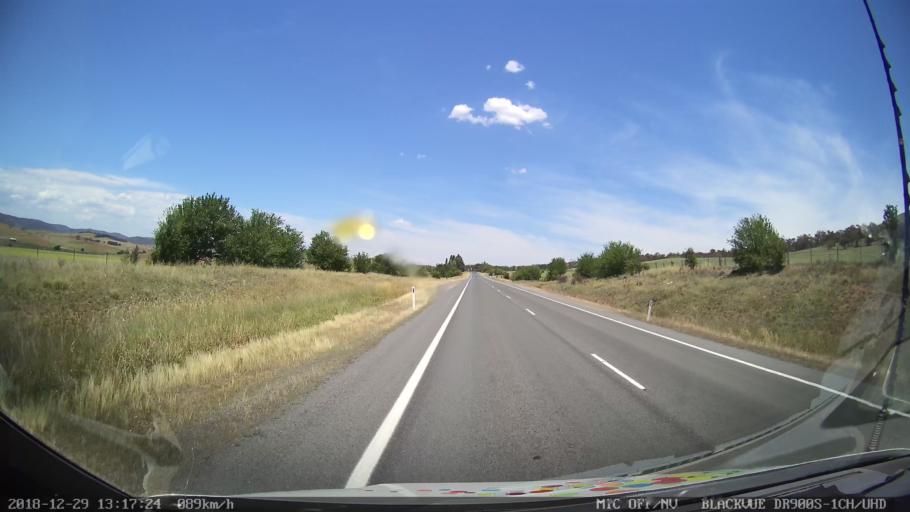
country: AU
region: Australian Capital Territory
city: Macarthur
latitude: -35.7369
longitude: 149.1608
